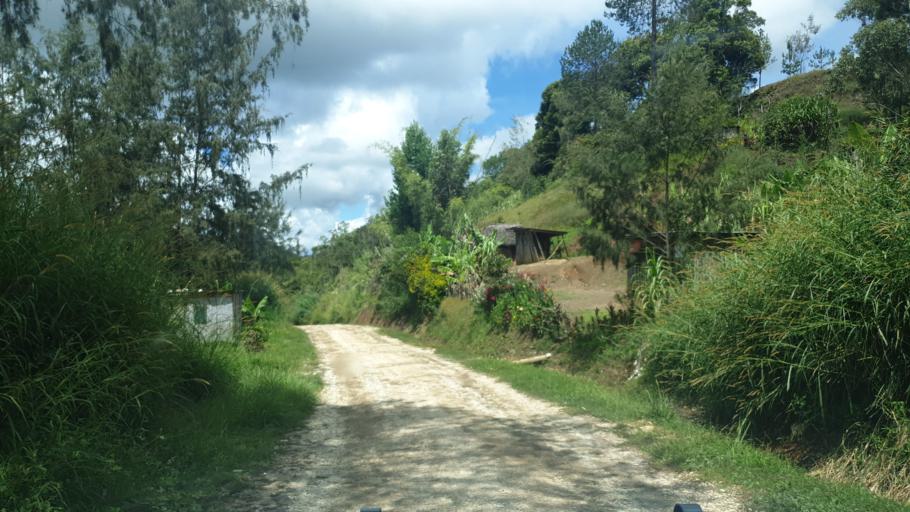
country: PG
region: Chimbu
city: Kundiawa
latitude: -6.2201
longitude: 145.1375
